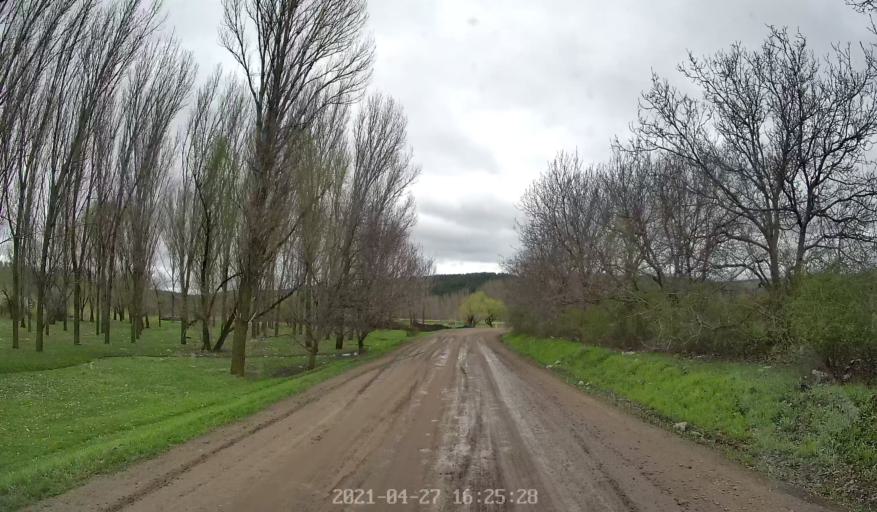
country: MD
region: Chisinau
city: Singera
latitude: 46.9849
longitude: 29.0221
